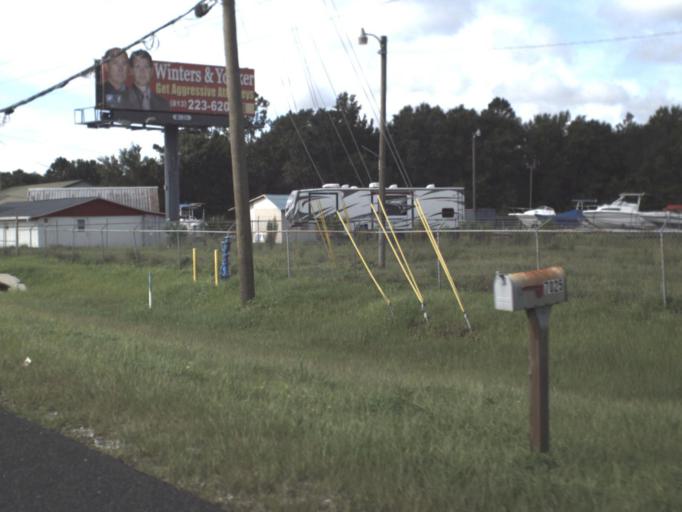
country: US
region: Florida
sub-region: Pasco County
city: Land O' Lakes
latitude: 28.2602
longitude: -82.4751
